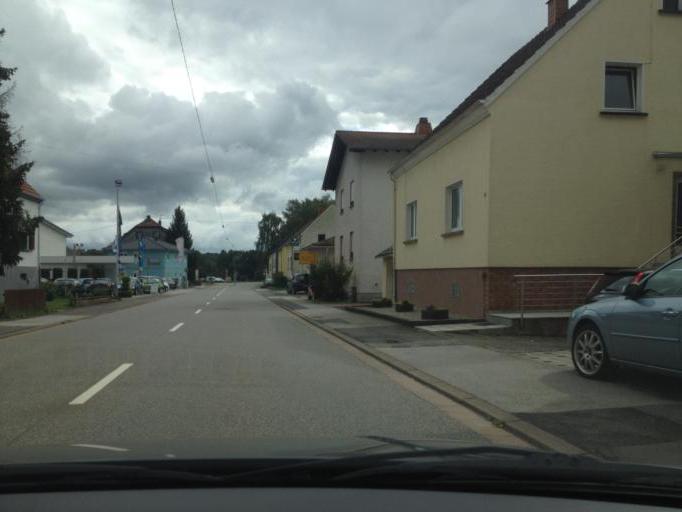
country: DE
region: Saarland
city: Oberthal
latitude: 49.5079
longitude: 7.0930
